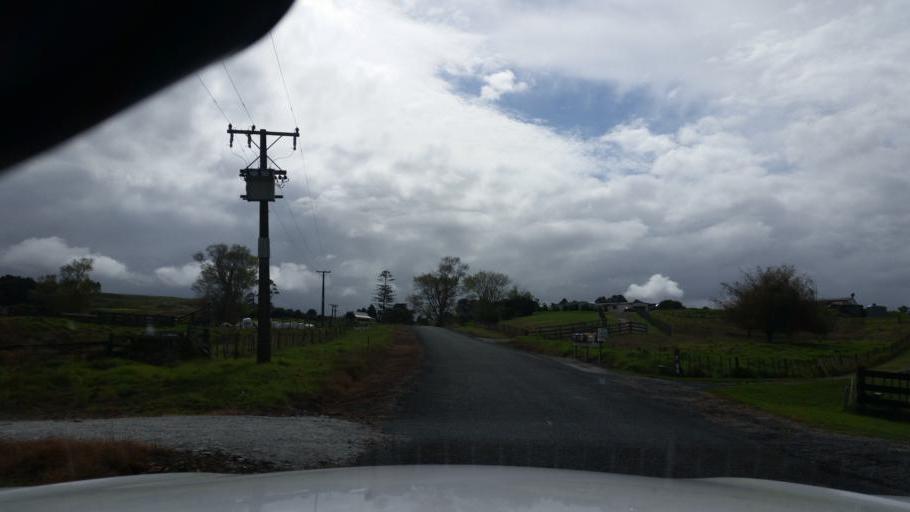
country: NZ
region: Northland
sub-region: Whangarei
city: Ruakaka
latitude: -36.1092
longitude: 174.2775
